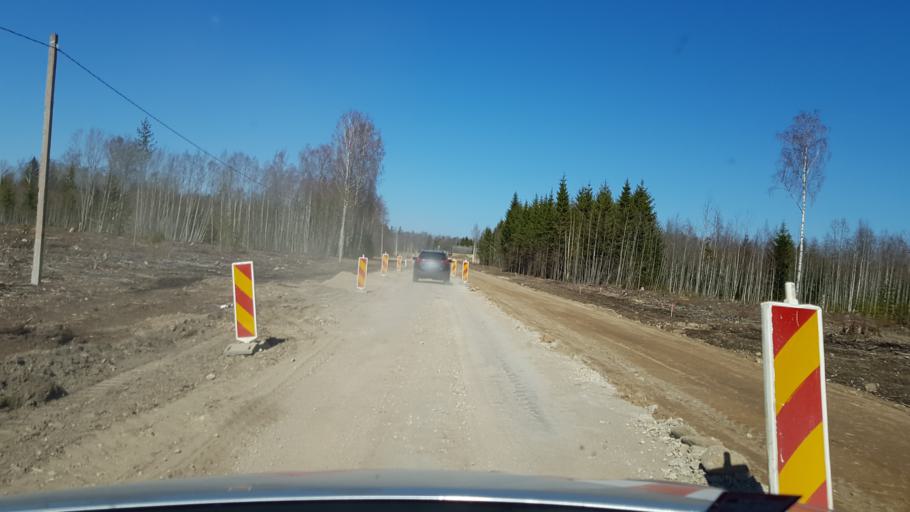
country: EE
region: Jogevamaa
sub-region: Mustvee linn
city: Mustvee
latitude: 59.0331
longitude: 26.6855
